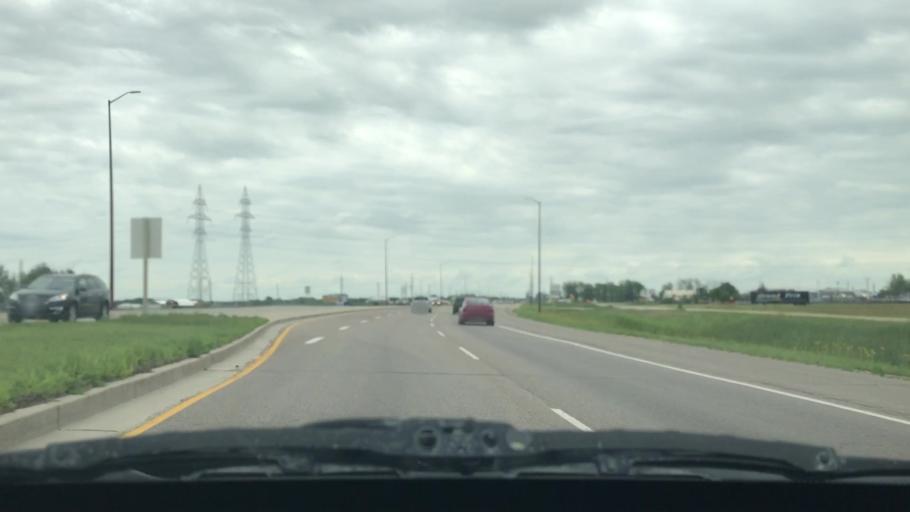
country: CA
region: Manitoba
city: Winnipeg
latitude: 49.8544
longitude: -97.0078
